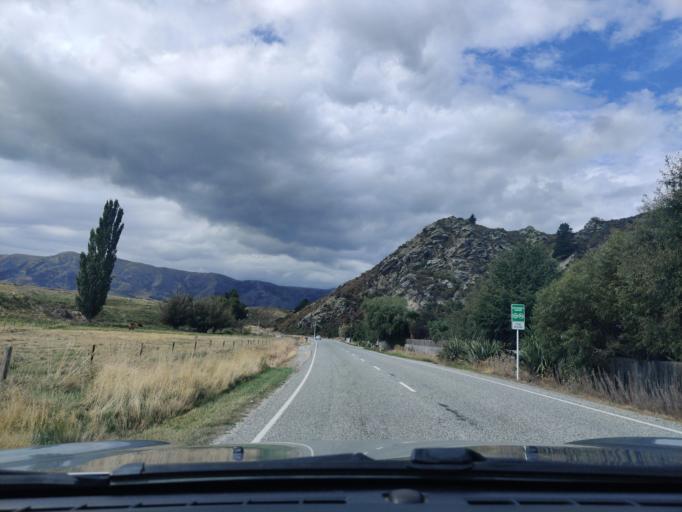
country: NZ
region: Otago
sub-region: Queenstown-Lakes District
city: Wanaka
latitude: -44.7517
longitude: 169.2840
